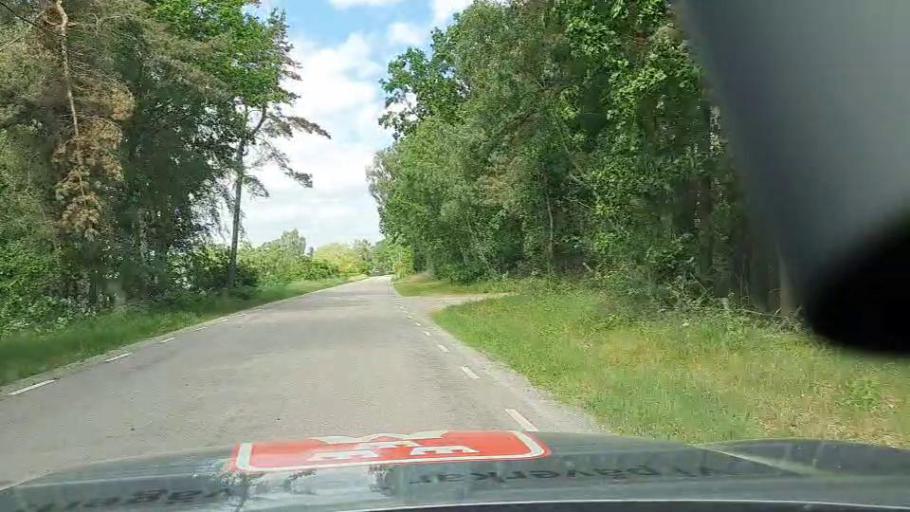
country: SE
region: Blekinge
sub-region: Karlshamns Kommun
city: Morrum
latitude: 56.1031
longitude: 14.6853
